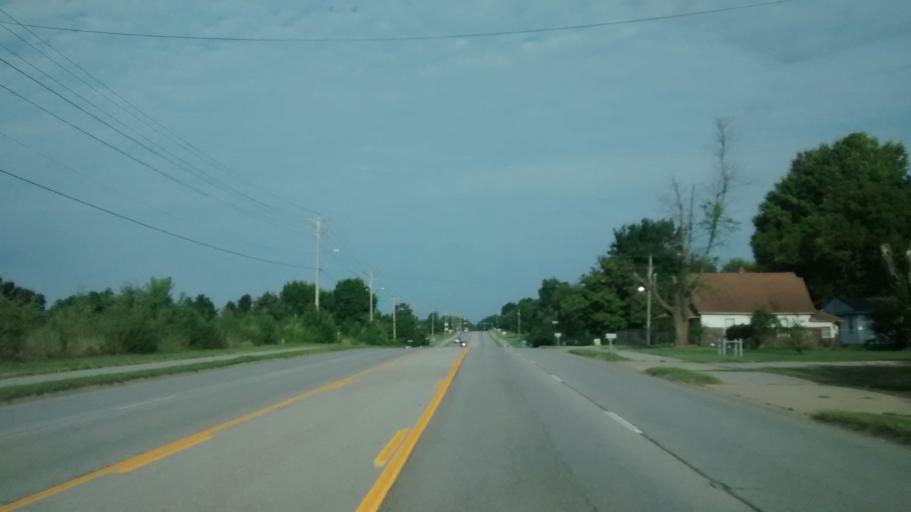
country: US
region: Arkansas
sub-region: Washington County
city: Farmington
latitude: 36.0792
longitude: -94.2454
